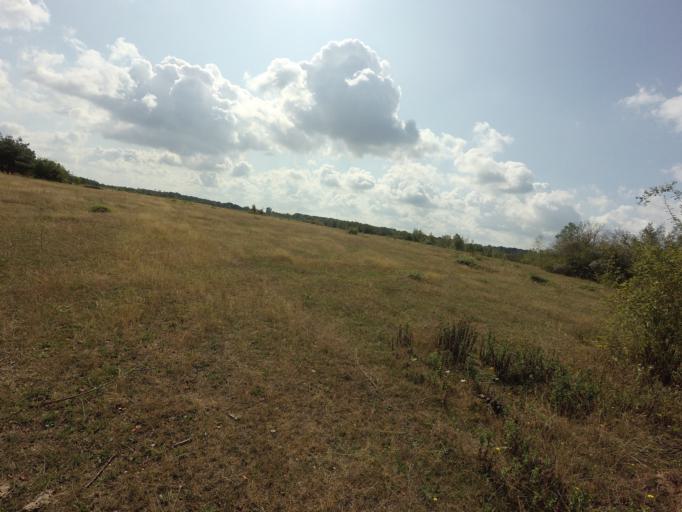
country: NL
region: Limburg
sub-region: Gemeente Brunssum
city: Brunssum
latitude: 50.9321
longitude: 6.0239
